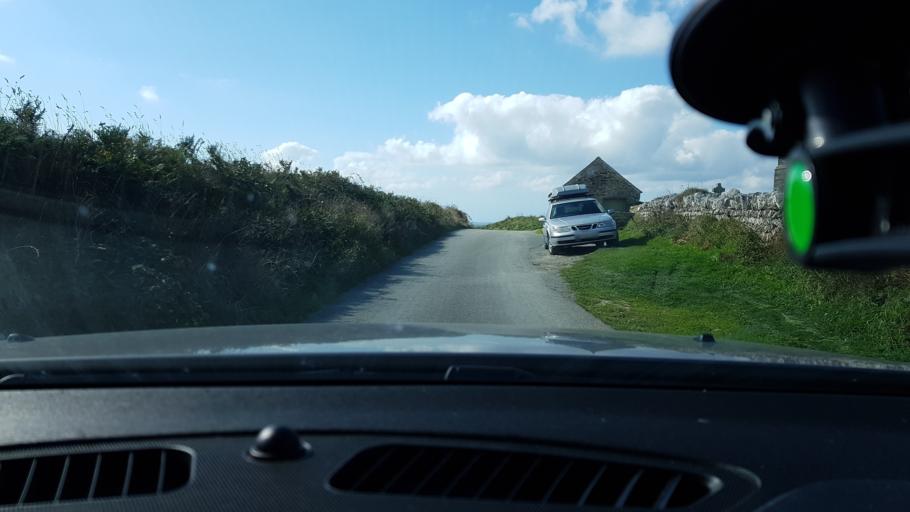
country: GB
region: England
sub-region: Cornwall
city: Tintagel
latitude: 50.6624
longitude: -4.7593
